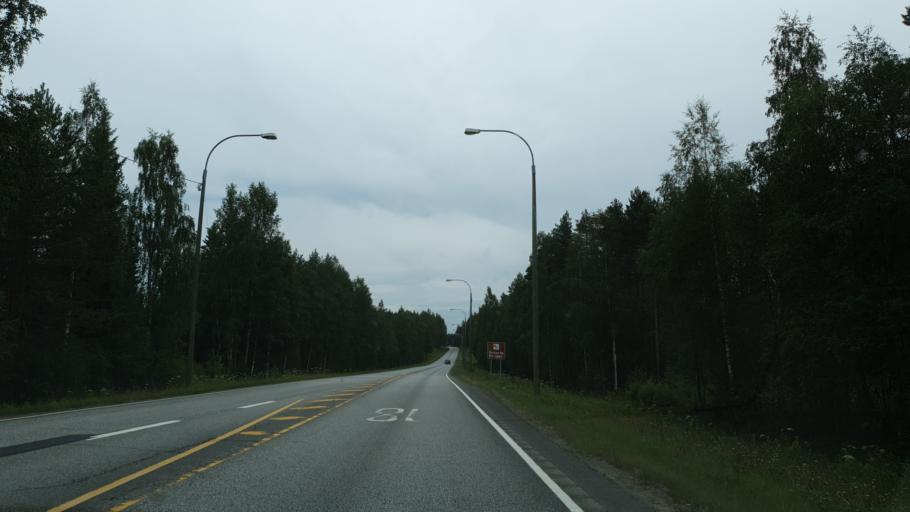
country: FI
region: North Karelia
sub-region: Joensuu
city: Pyhaeselkae
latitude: 62.4459
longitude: 30.0164
